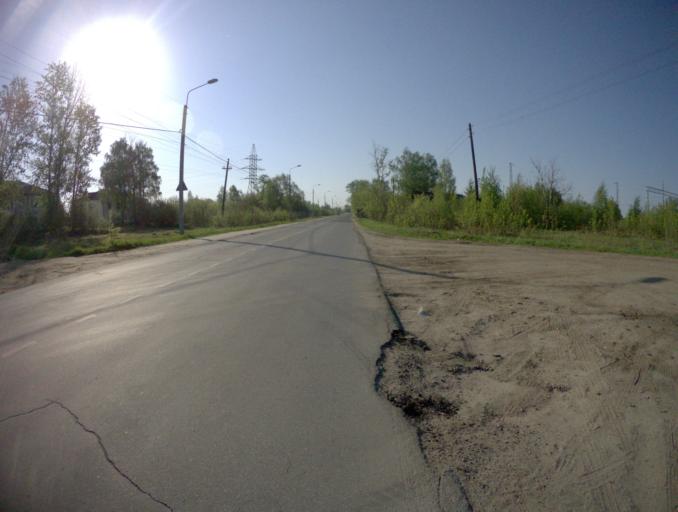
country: RU
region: Vladimir
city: Novovyazniki
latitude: 56.2061
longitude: 42.1640
